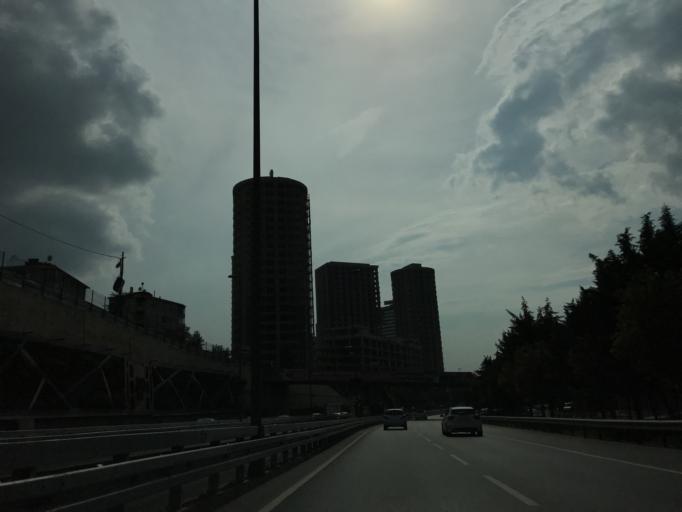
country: TR
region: Istanbul
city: UEskuedar
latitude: 40.9951
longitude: 29.0507
